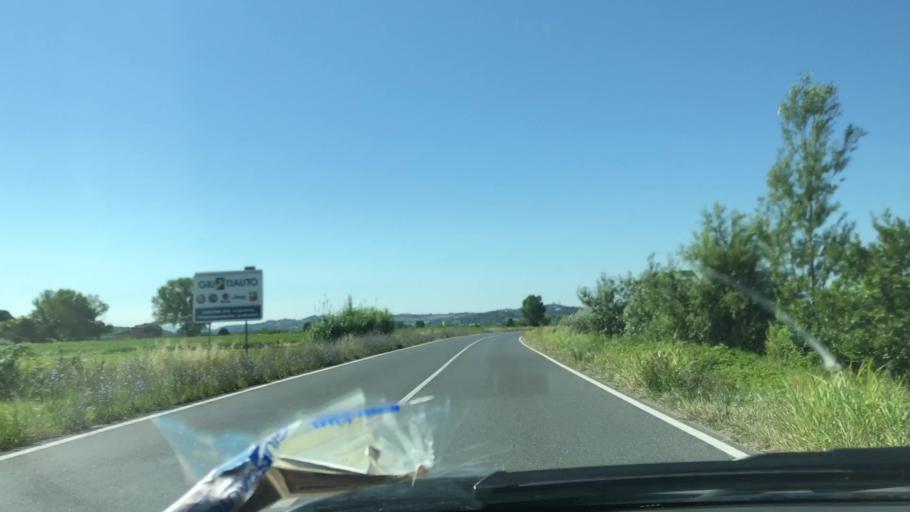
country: IT
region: Tuscany
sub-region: Province of Pisa
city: Forcoli
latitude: 43.5918
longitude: 10.7002
